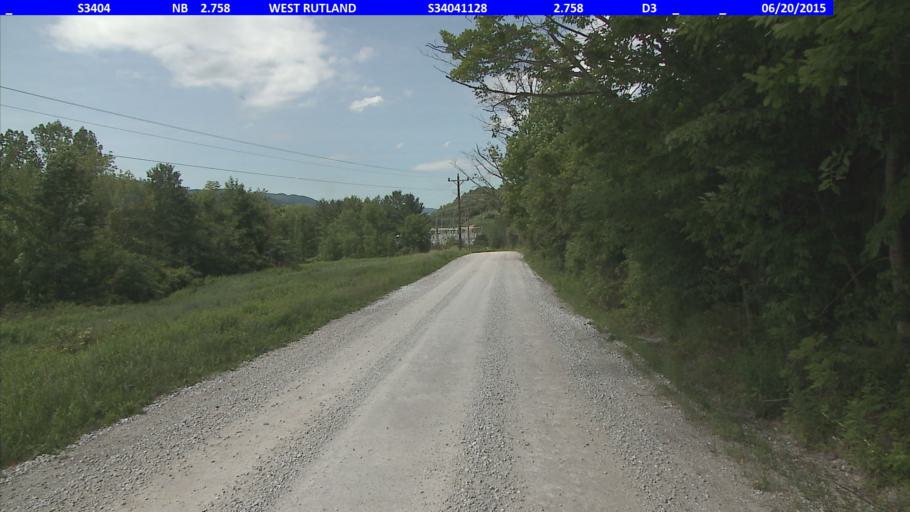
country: US
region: Vermont
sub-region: Rutland County
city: West Rutland
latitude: 43.6301
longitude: -73.0560
